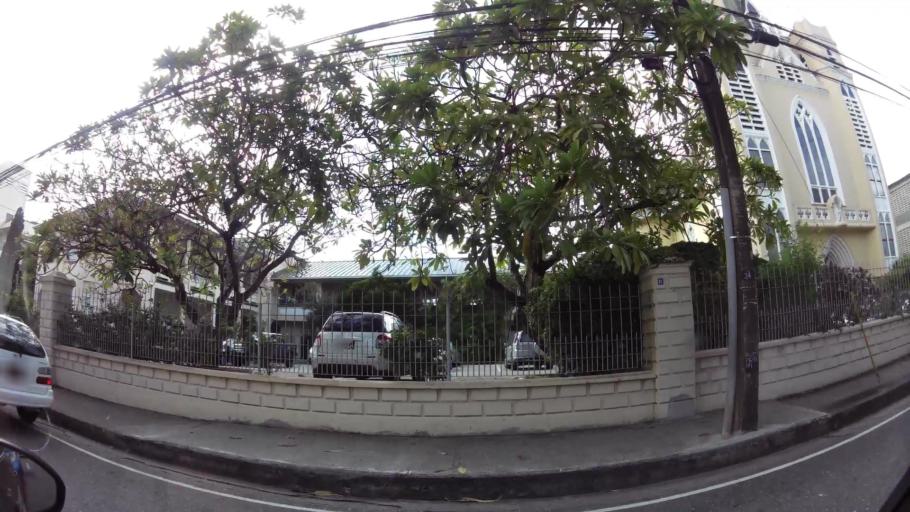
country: TT
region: City of Port of Spain
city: Port-of-Spain
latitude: 10.6588
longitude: -61.5099
